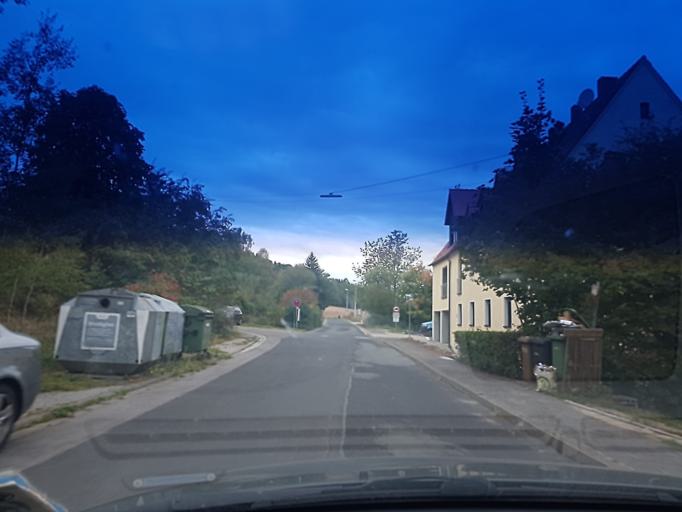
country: DE
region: Bavaria
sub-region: Regierungsbezirk Unterfranken
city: Geiselwind
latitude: 49.8403
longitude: 10.5164
